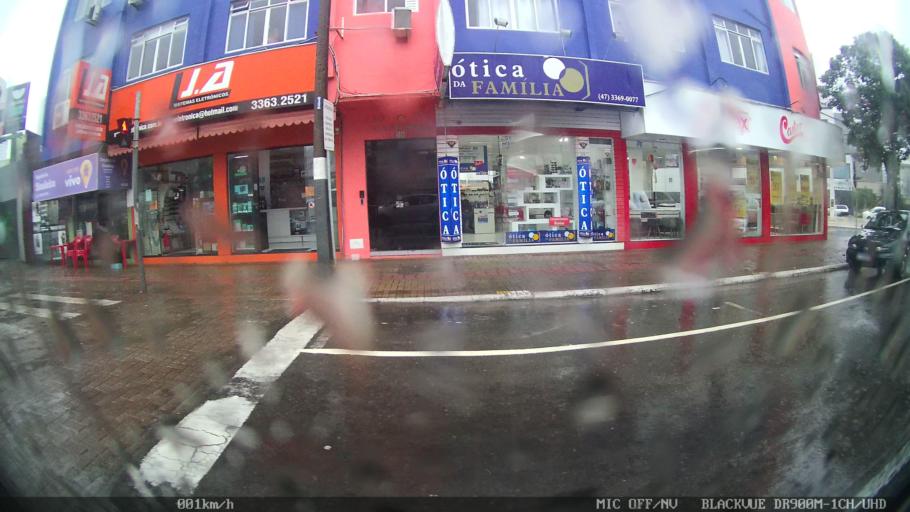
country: BR
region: Santa Catarina
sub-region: Balneario Camboriu
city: Balneario Camboriu
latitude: -26.9876
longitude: -48.6396
